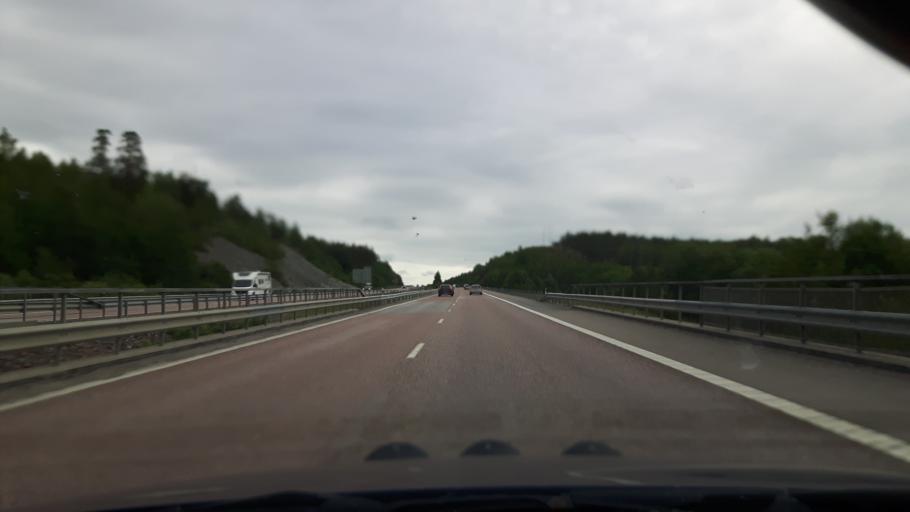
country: SE
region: Soedermanland
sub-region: Strangnas Kommun
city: Mariefred
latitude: 59.2404
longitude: 17.1785
